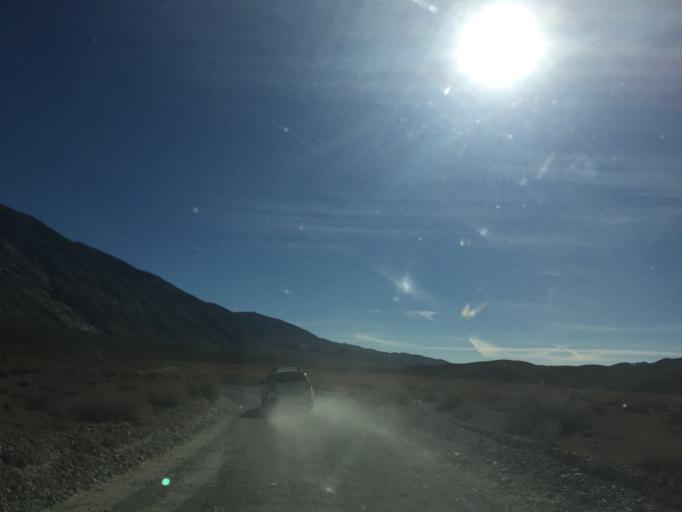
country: US
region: California
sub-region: Inyo County
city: Lone Pine
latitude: 36.8590
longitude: -117.5034
